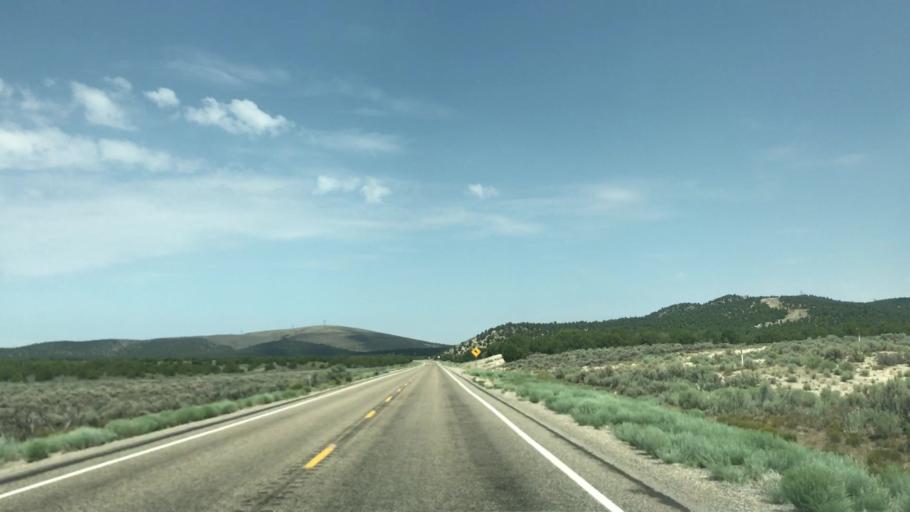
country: US
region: Nevada
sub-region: White Pine County
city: Ely
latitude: 39.3758
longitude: -115.0618
